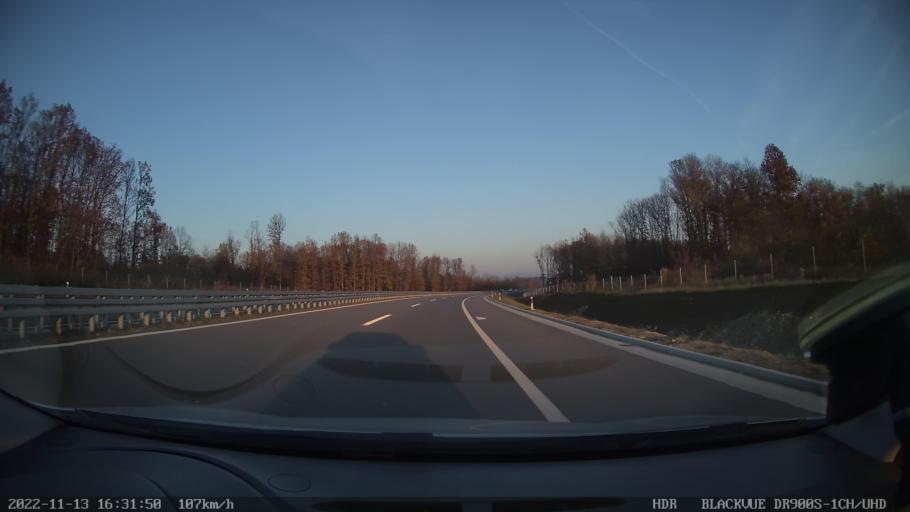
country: RS
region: Central Serbia
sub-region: Moravicki Okrug
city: Cacak
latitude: 43.9137
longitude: 20.2785
